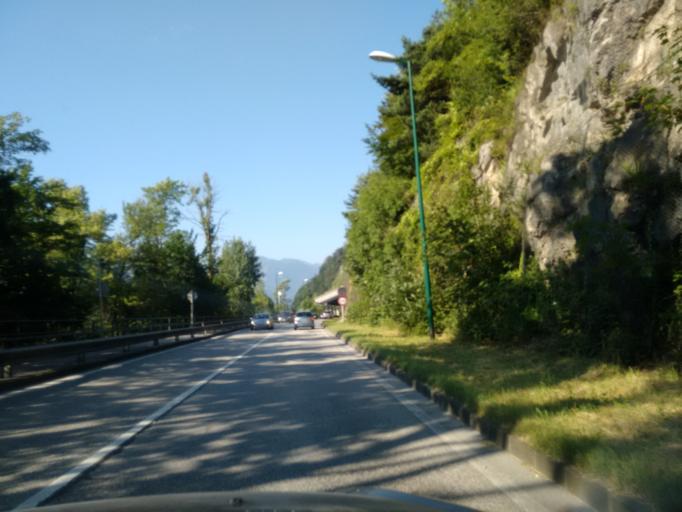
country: AT
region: Upper Austria
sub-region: Politischer Bezirk Gmunden
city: Ebensee
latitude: 47.8284
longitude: 13.7906
